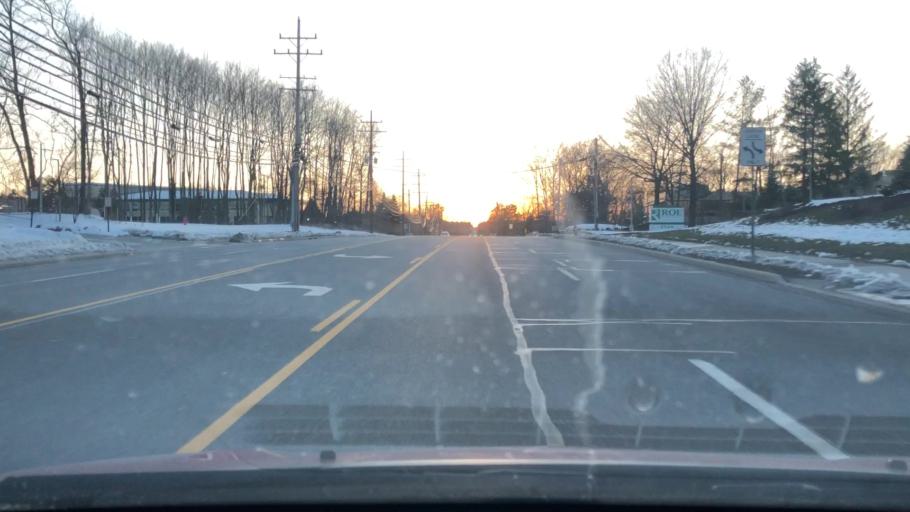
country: US
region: Ohio
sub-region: Cuyahoga County
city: Independence
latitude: 41.3620
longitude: -81.6310
